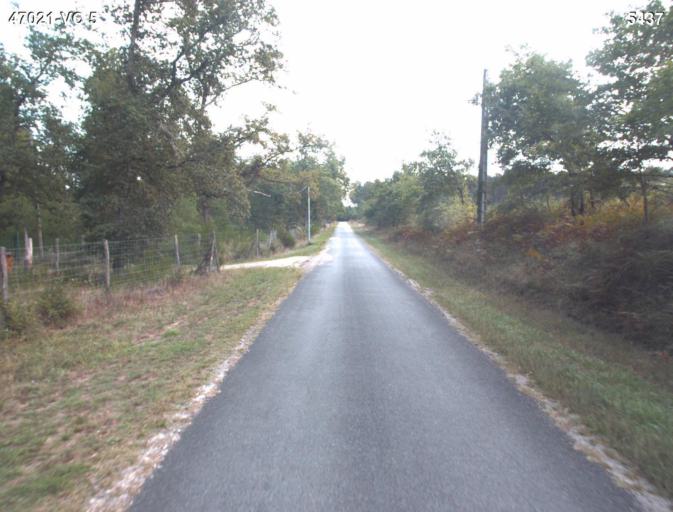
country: FR
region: Aquitaine
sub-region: Departement du Lot-et-Garonne
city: Barbaste
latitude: 44.1479
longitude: 0.2330
